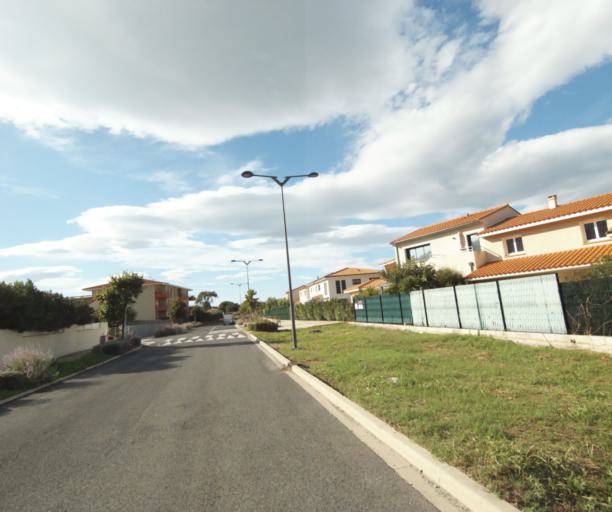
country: FR
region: Languedoc-Roussillon
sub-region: Departement des Pyrenees-Orientales
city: Argelers
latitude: 42.5437
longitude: 3.0386
